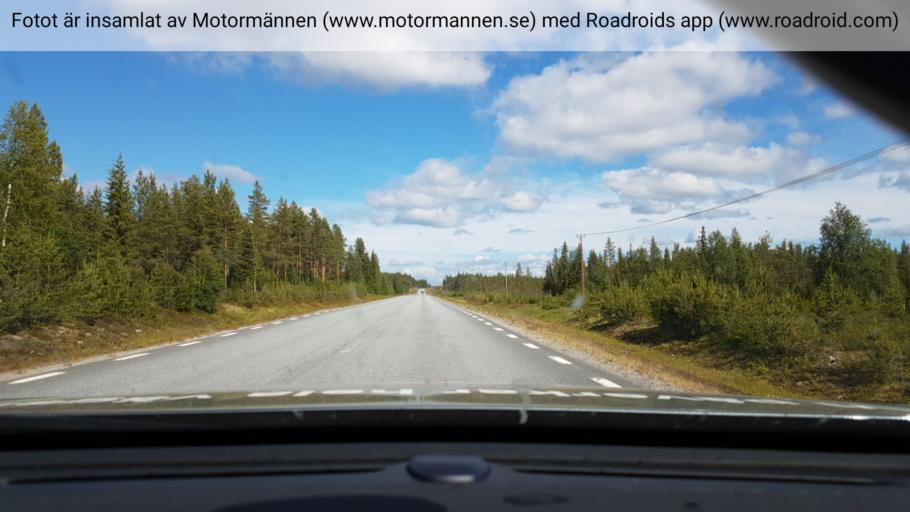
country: SE
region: Vaesterbotten
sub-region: Sorsele Kommun
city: Sorsele
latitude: 65.5572
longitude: 17.7657
